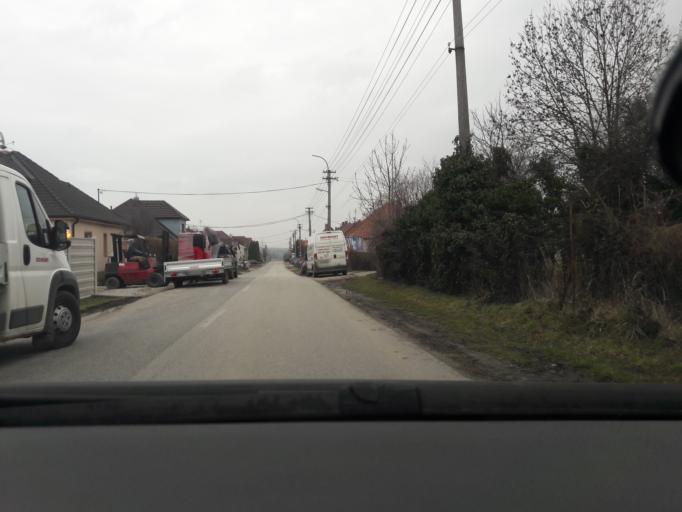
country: SK
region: Bratislavsky
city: Modra
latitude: 48.4009
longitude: 17.3643
